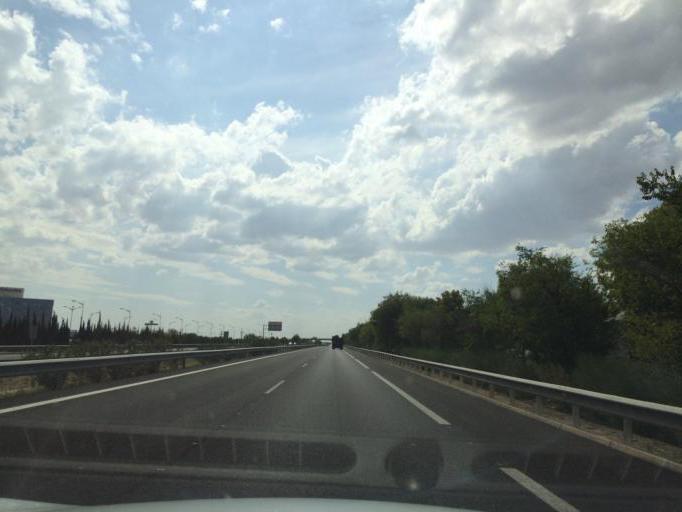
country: ES
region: Castille-La Mancha
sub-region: Provincia de Albacete
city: Albacete
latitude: 39.0099
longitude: -1.8808
